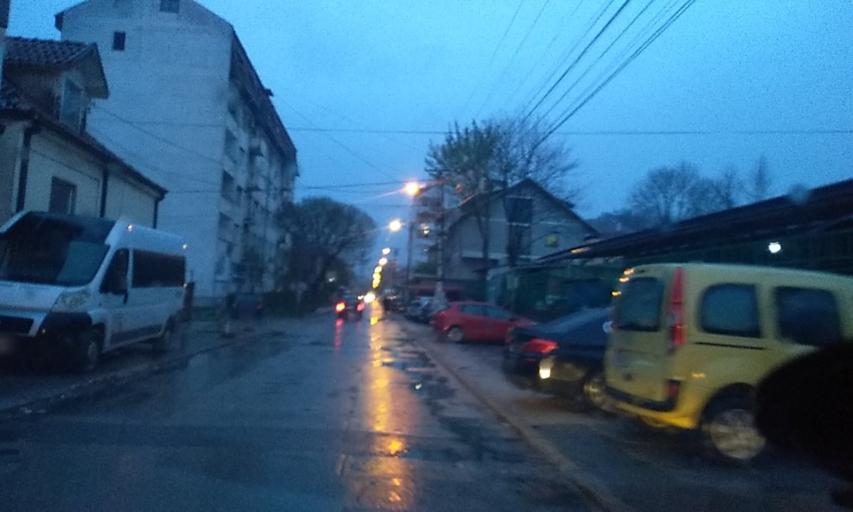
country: RS
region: Central Serbia
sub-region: Nisavski Okrug
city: Nis
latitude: 43.3138
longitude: 21.8840
